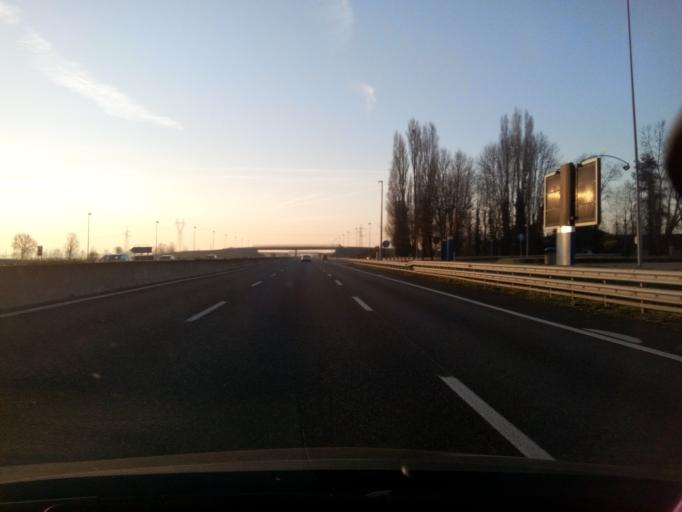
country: IT
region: Lombardy
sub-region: Provincia di Lodi
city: Mairano
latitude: 45.3207
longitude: 9.3769
